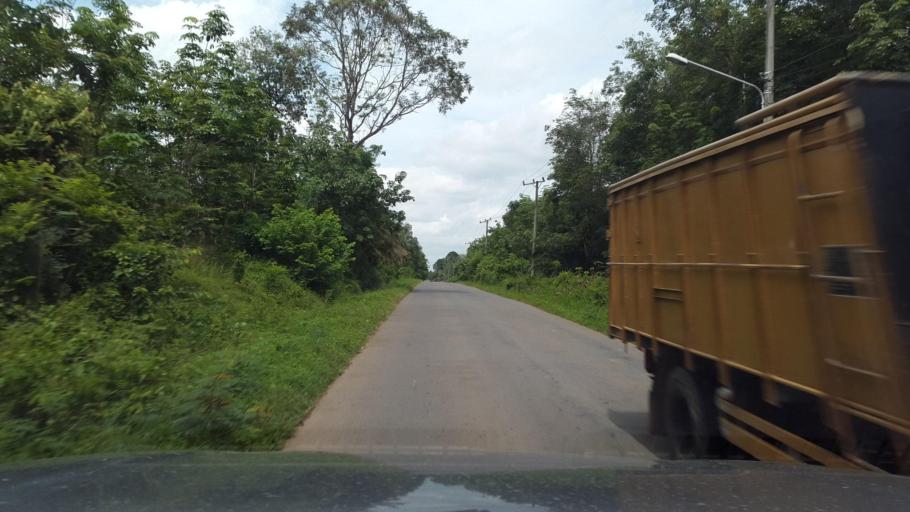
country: ID
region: South Sumatra
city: Gunungmegang Dalam
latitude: -3.3652
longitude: 103.9390
